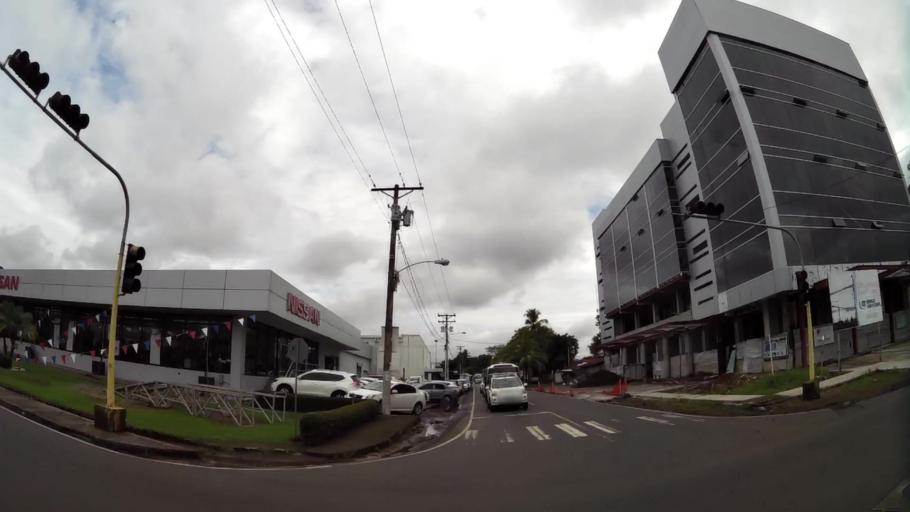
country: PA
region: Chiriqui
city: David
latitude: 8.4256
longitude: -82.4346
